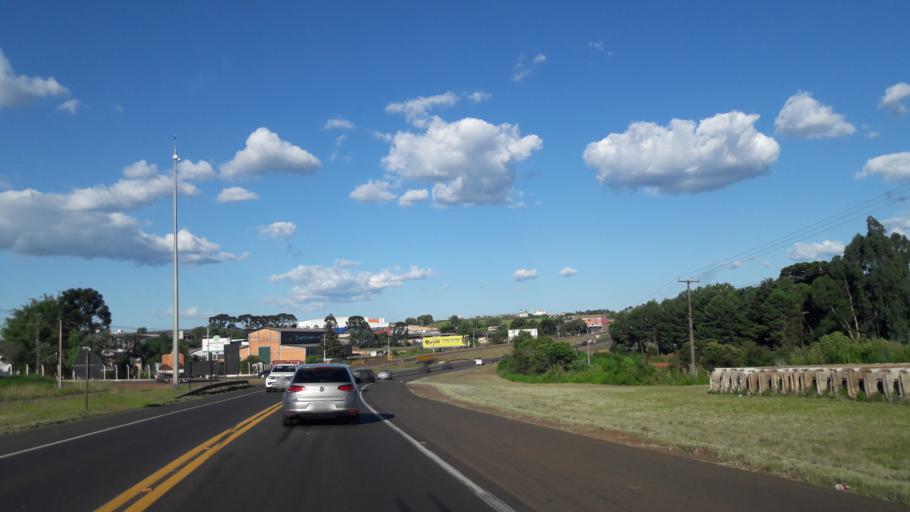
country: BR
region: Parana
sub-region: Guarapuava
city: Guarapuava
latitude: -25.3669
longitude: -51.4928
